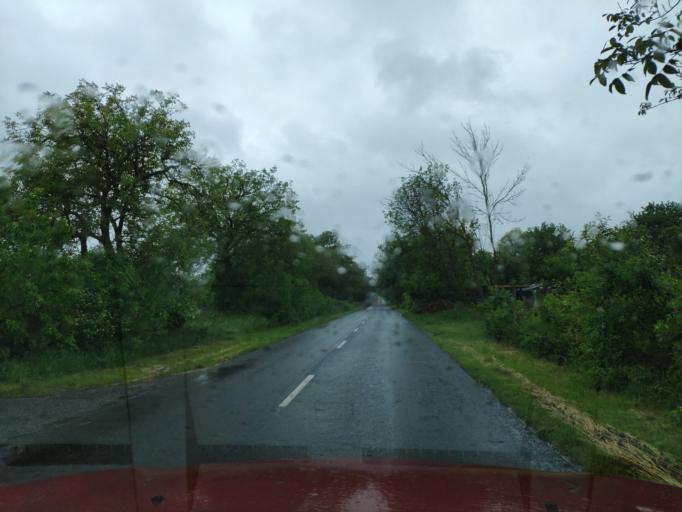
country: SK
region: Kosicky
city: Cierna nad Tisou
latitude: 48.4221
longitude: 22.1016
